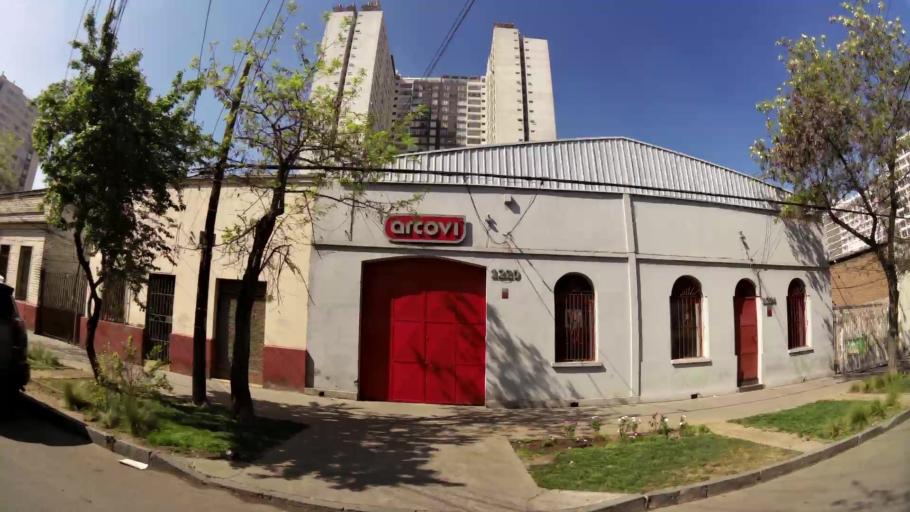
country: CL
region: Santiago Metropolitan
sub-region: Provincia de Santiago
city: Santiago
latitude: -33.4575
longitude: -70.6308
